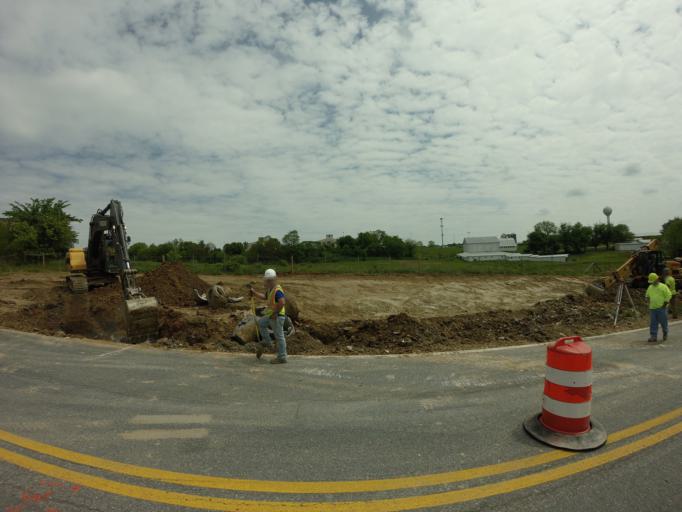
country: US
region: Maryland
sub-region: Frederick County
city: Urbana
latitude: 39.3244
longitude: -77.3420
